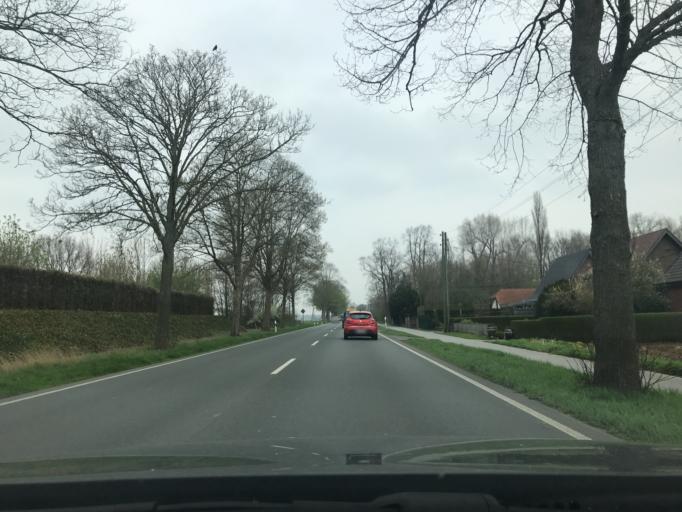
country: DE
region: North Rhine-Westphalia
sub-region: Regierungsbezirk Dusseldorf
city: Weeze
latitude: 51.6375
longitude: 6.1926
